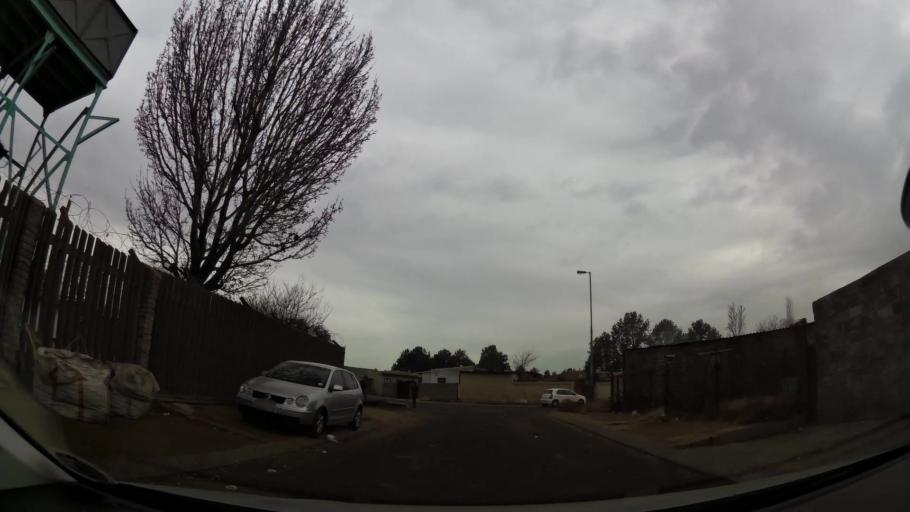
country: ZA
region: Gauteng
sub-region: City of Johannesburg Metropolitan Municipality
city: Soweto
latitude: -26.2529
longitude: 27.8724
